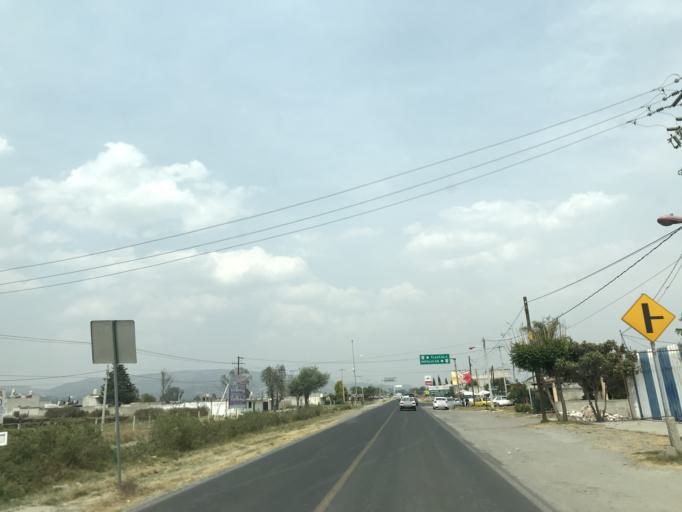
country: MX
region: Tlaxcala
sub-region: Ixtacuixtla de Mariano Matamoros
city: Santa Justina Ecatepec
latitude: 19.3114
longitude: -98.3454
